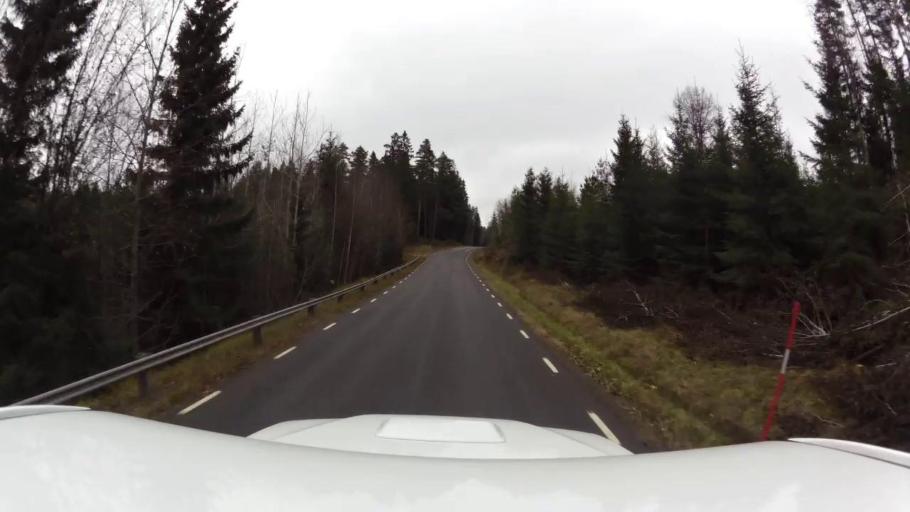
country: SE
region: OEstergoetland
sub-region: Kinda Kommun
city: Rimforsa
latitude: 58.1426
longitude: 15.4549
